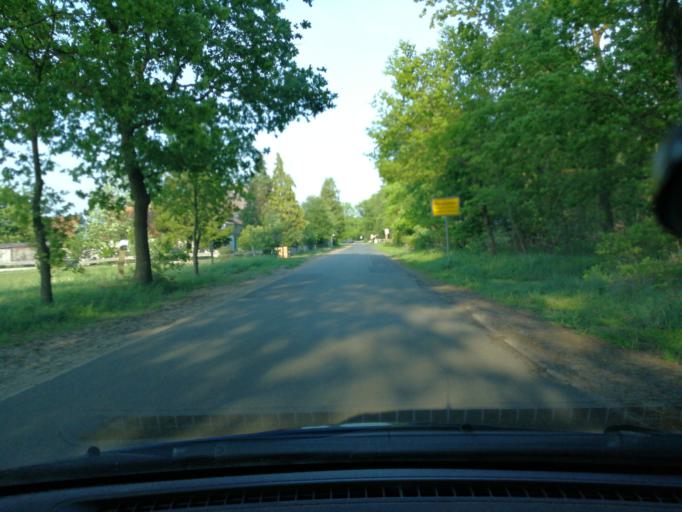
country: DE
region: Lower Saxony
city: Ludersburg
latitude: 53.2898
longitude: 10.5668
